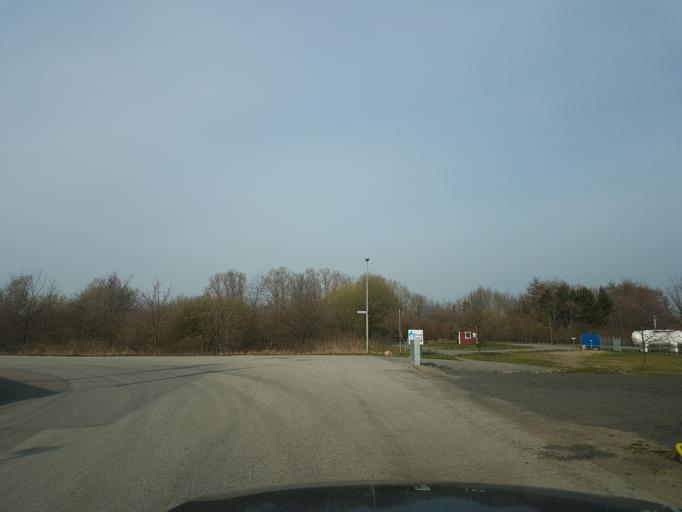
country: SE
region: Skane
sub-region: Ystads Kommun
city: Ystad
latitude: 55.4475
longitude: 13.8499
